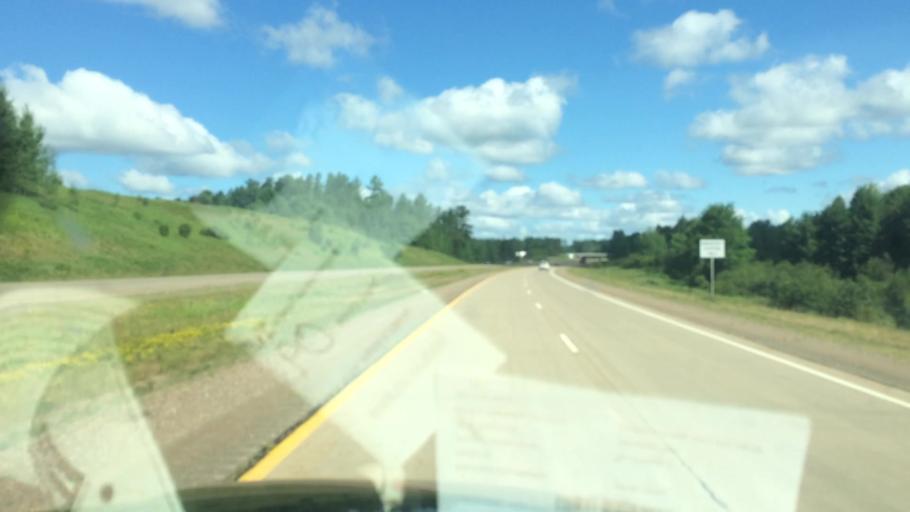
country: US
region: Wisconsin
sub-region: Lincoln County
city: Tomahawk
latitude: 45.4275
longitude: -89.6772
